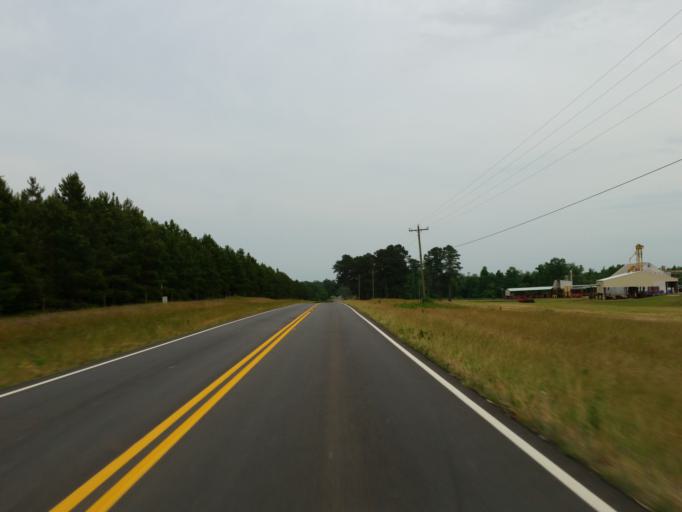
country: US
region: Georgia
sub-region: Dooly County
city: Unadilla
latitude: 32.2827
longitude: -83.7457
